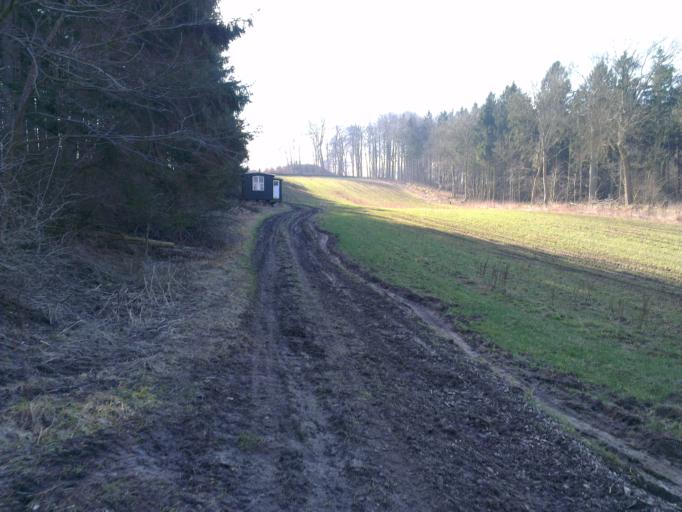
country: DK
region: Capital Region
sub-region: Frederikssund Kommune
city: Skibby
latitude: 55.7836
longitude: 11.9560
